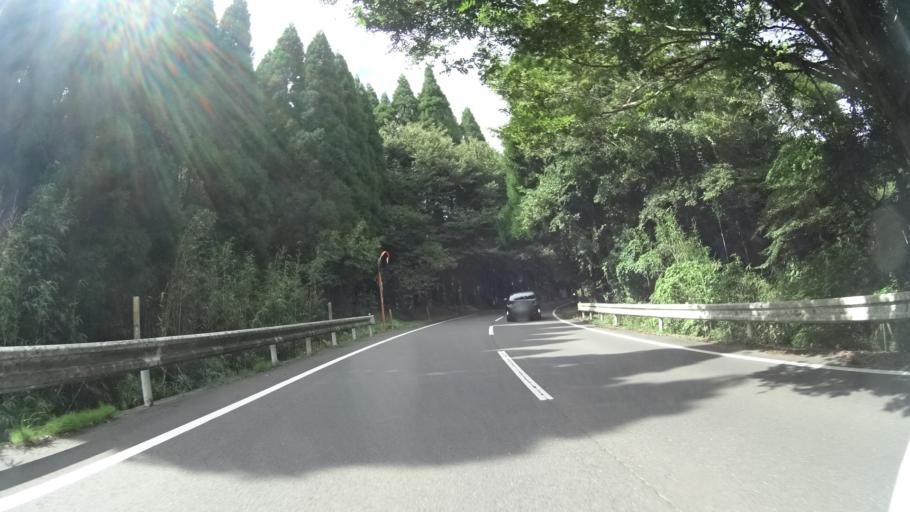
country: JP
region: Oita
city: Beppu
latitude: 33.3026
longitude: 131.3920
